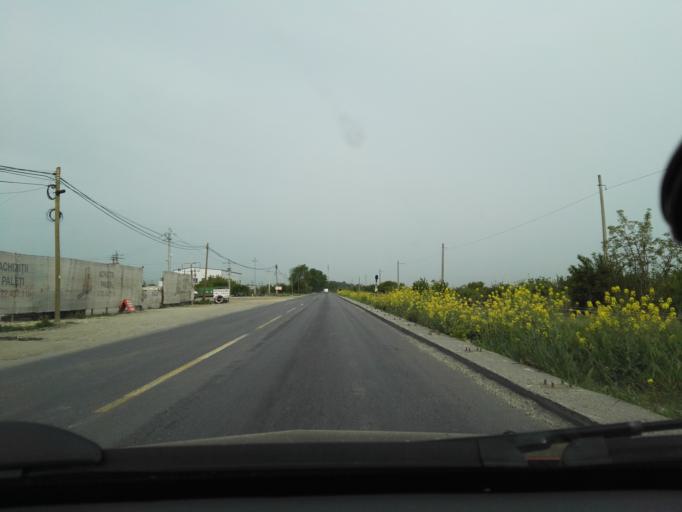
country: RO
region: Ilfov
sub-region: Comuna Magurele
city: Magurele
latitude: 44.3594
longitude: 26.0360
